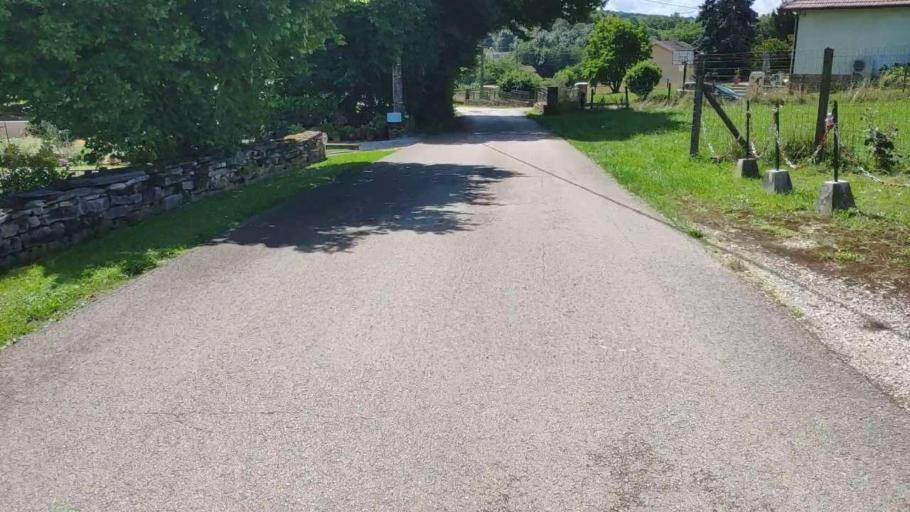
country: FR
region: Franche-Comte
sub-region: Departement du Jura
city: Bletterans
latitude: 46.8308
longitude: 5.5584
